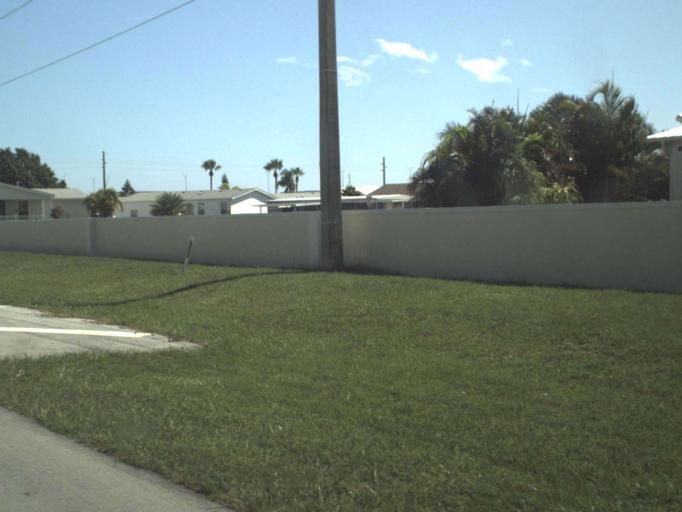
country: US
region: Florida
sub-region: Indian River County
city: Vero Beach
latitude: 27.6289
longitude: -80.3786
